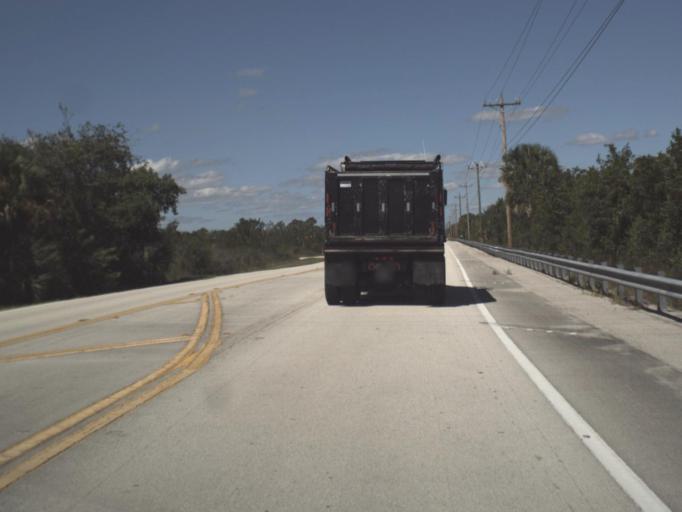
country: US
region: Florida
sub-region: Collier County
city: Marco
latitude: 25.9740
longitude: -81.5531
